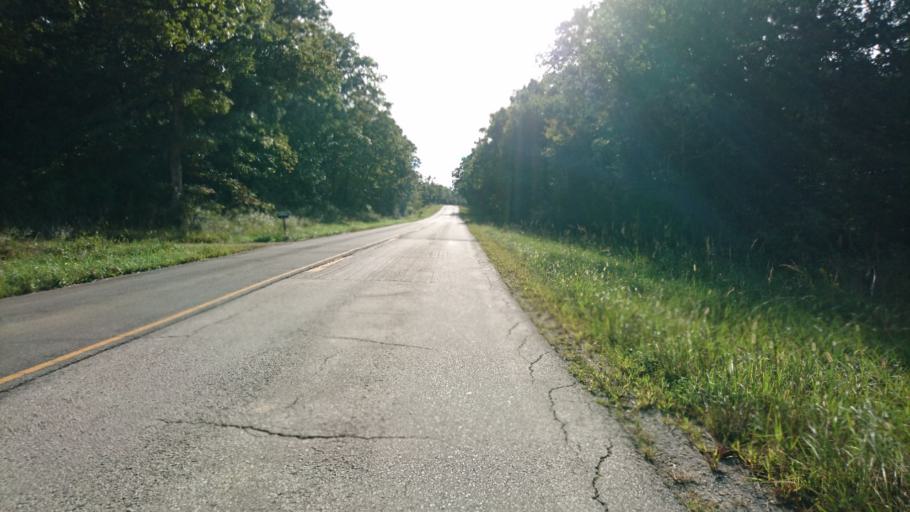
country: US
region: Missouri
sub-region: Crawford County
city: Cuba
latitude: 38.0995
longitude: -91.3530
